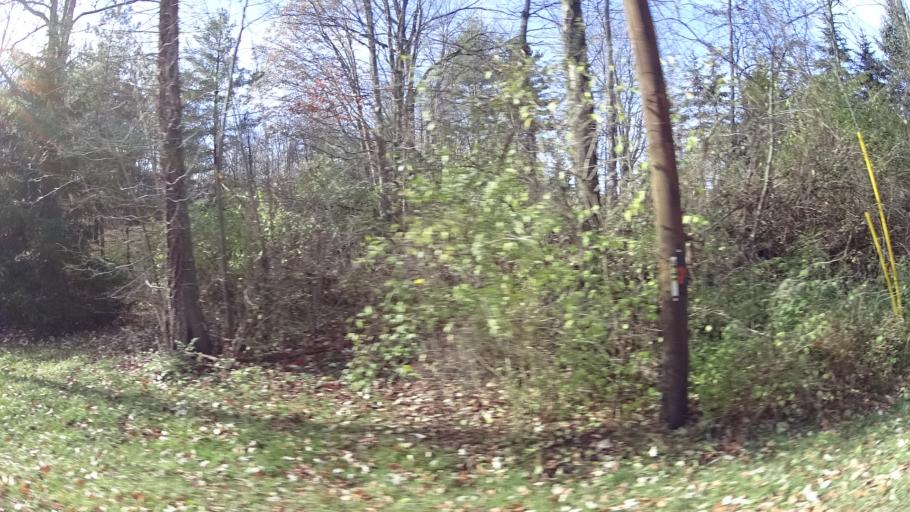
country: US
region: Ohio
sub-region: Lorain County
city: Wellington
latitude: 41.0926
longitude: -82.2398
